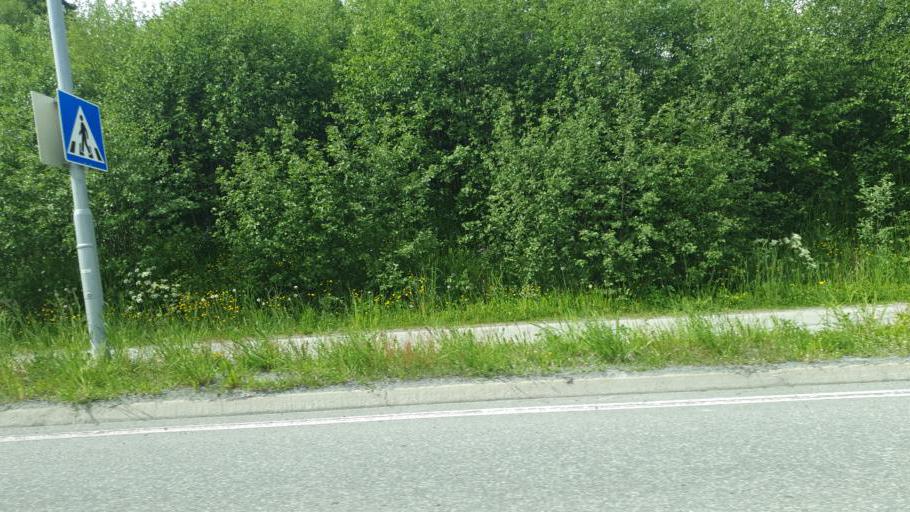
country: NO
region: Nord-Trondelag
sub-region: Leksvik
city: Leksvik
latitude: 63.6671
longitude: 10.6073
